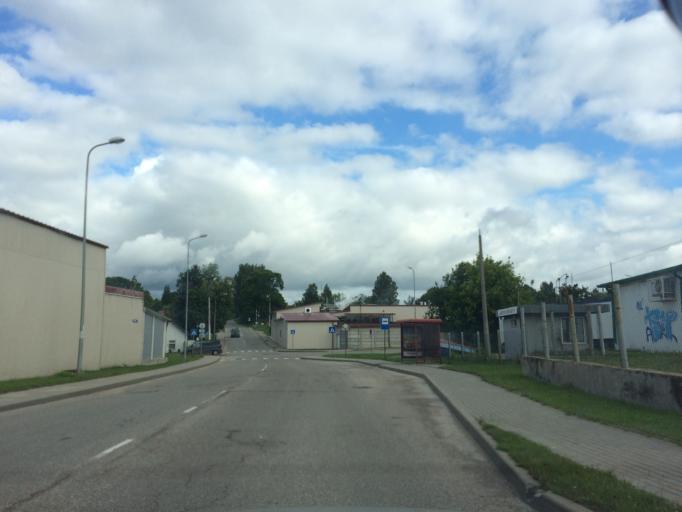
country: LV
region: Rezekne
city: Rezekne
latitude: 56.5128
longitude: 27.3247
